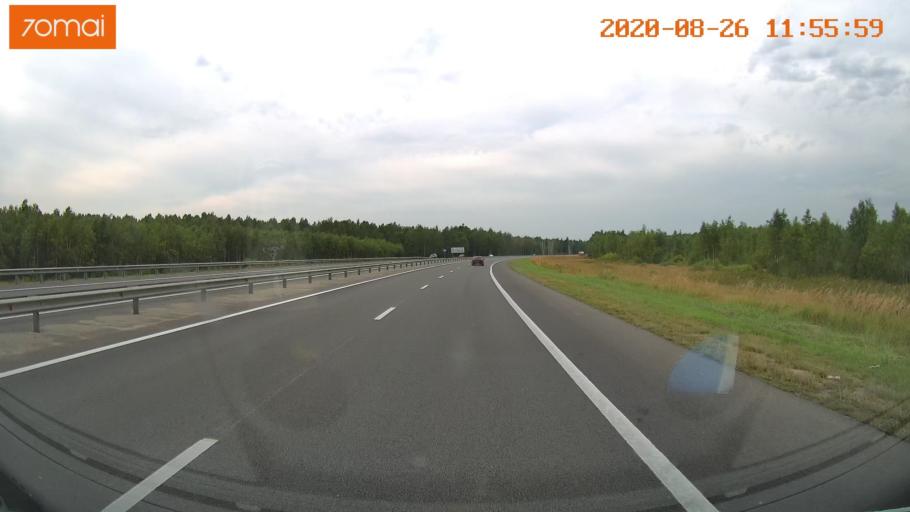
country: RU
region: Rjazan
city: Kiritsy
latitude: 54.2660
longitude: 40.3871
